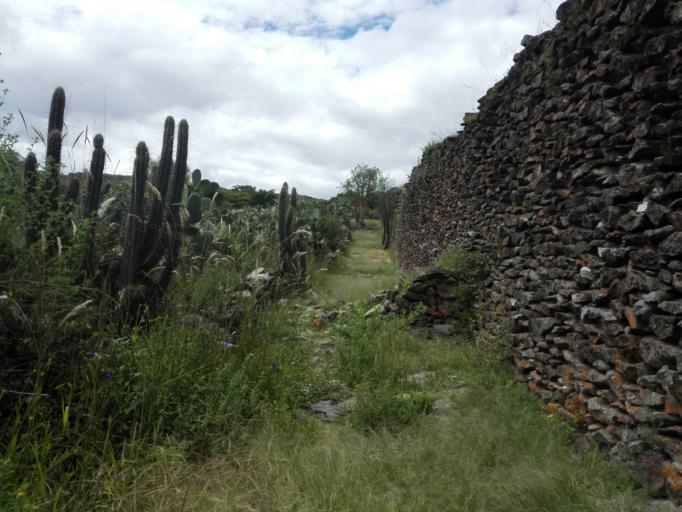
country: PE
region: Ayacucho
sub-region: Provincia de Huamanga
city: Pacaycasa
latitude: -13.0579
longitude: -74.1981
